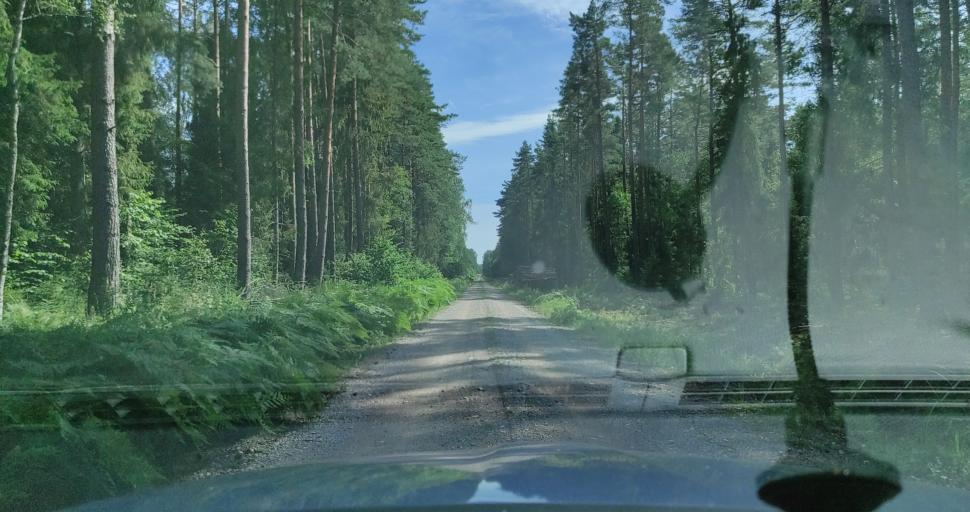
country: LV
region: Pavilostas
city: Pavilosta
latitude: 56.7774
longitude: 21.2880
